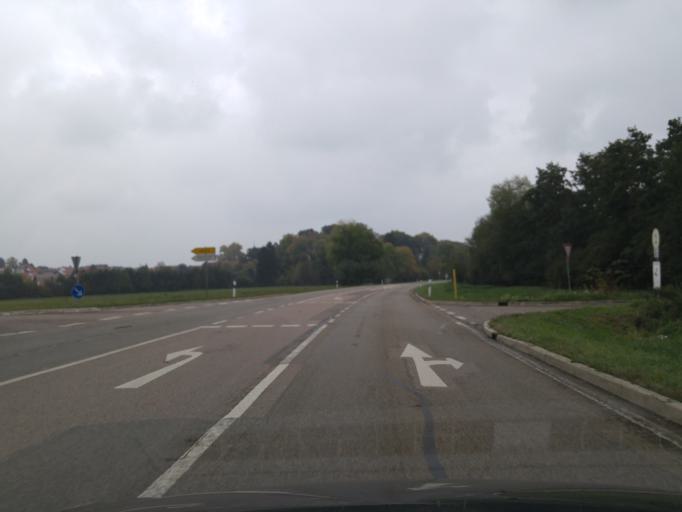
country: DE
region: Baden-Wuerttemberg
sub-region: Regierungsbezirk Stuttgart
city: Bad Rappenau
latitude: 49.2119
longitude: 9.0854
